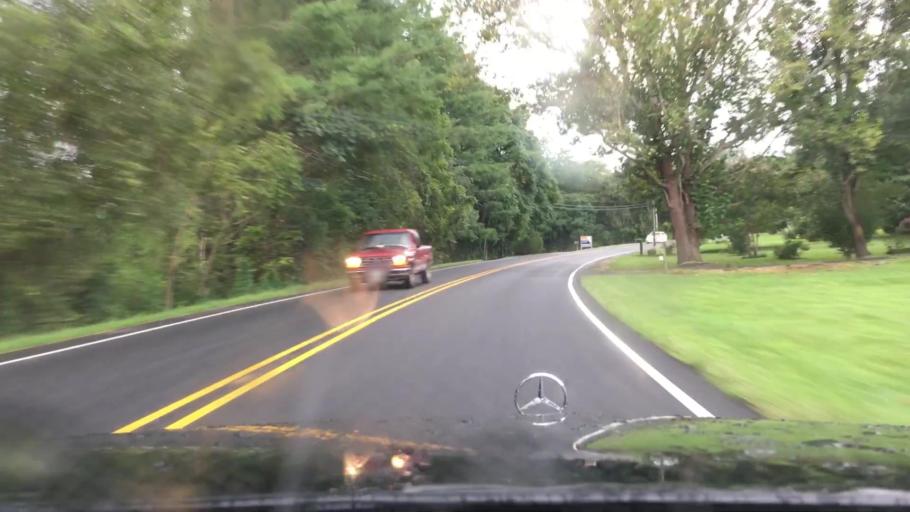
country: US
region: Virginia
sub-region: Nelson County
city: Nellysford
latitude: 37.8880
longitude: -78.8769
